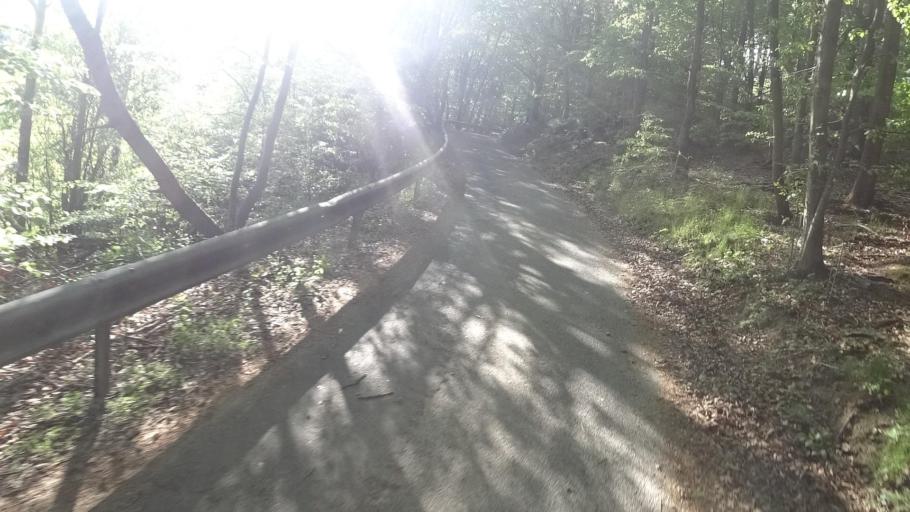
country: DE
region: Rheinland-Pfalz
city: Kirchsahr
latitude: 50.5085
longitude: 6.8712
